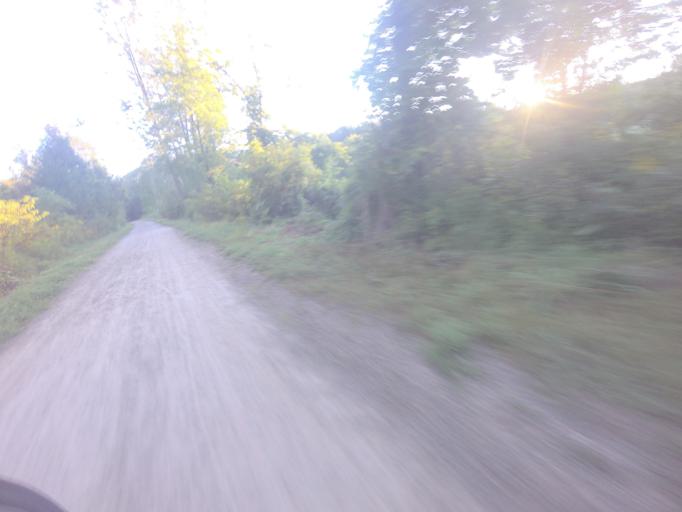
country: CA
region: Ontario
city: Bradford West Gwillimbury
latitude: 44.0145
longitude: -79.8072
